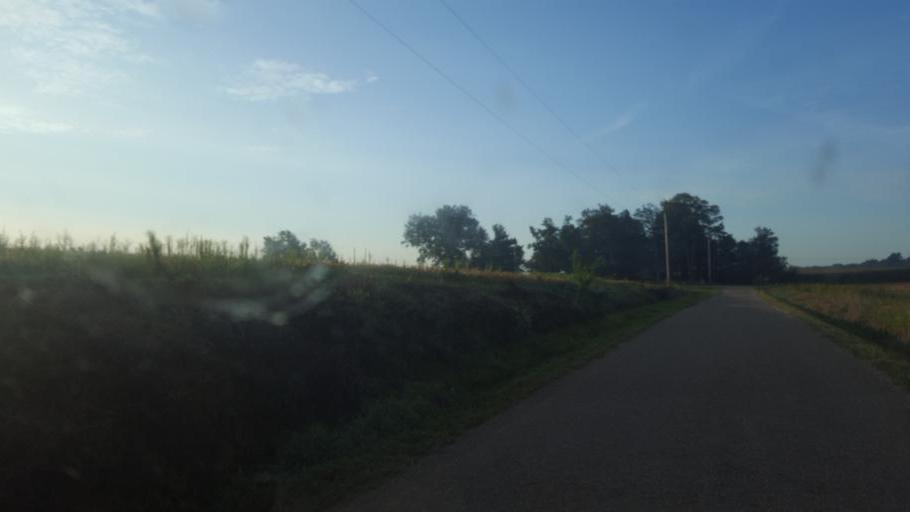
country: US
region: Ohio
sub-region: Knox County
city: Fredericktown
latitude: 40.4261
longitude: -82.6128
